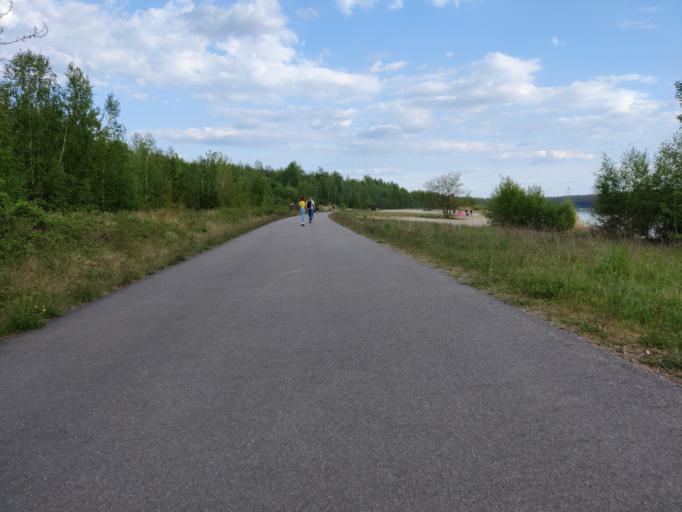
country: DE
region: Saxony
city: Rotha
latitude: 51.2242
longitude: 12.4392
